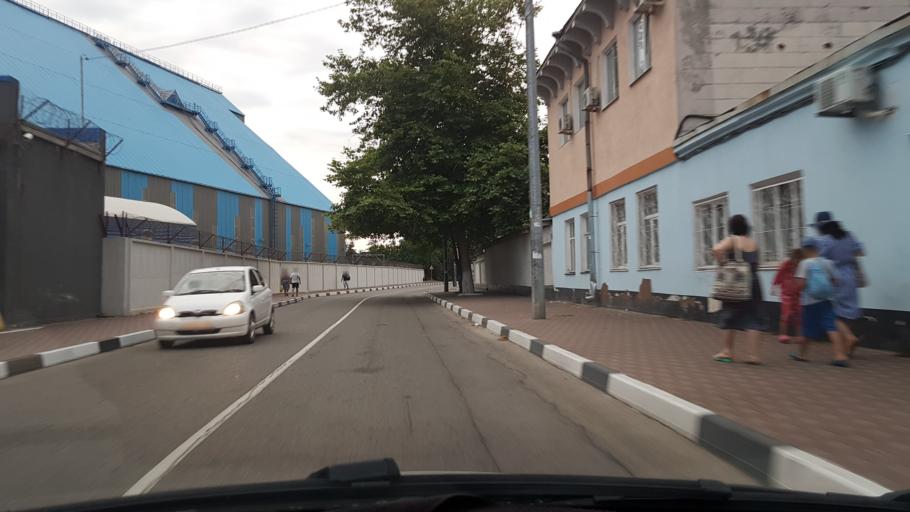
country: RU
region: Krasnodarskiy
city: Tuapse
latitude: 44.0939
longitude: 39.0785
